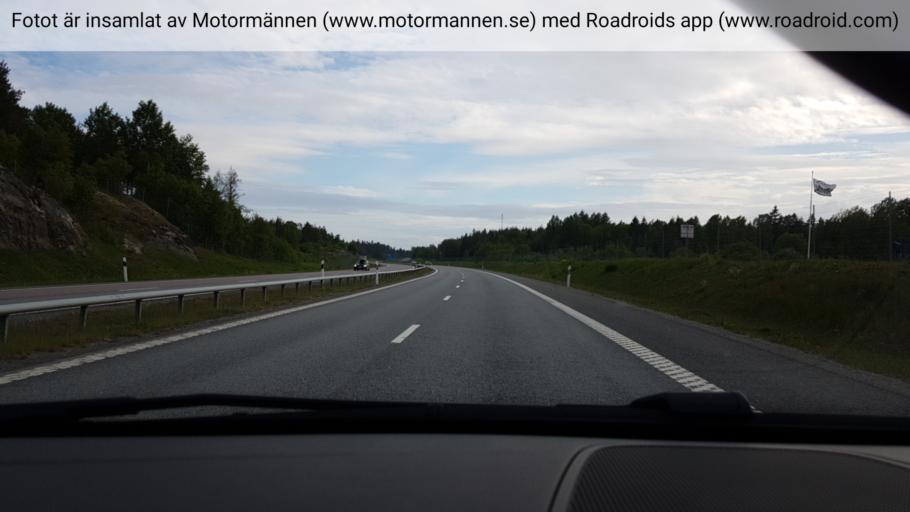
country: SE
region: Stockholm
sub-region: Haninge Kommun
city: Jordbro
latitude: 59.0855
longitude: 18.0826
